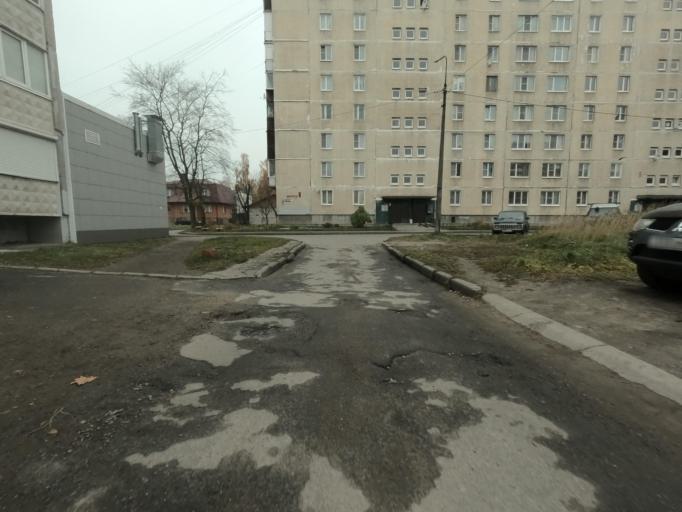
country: RU
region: Leningrad
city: Kirovsk
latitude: 59.8845
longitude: 30.9891
